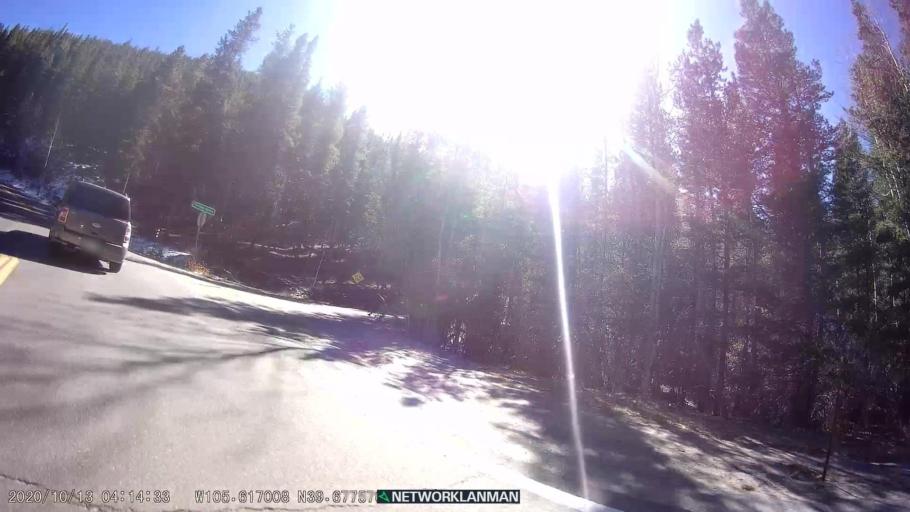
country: US
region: Colorado
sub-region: Clear Creek County
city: Georgetown
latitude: 39.6775
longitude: -105.6169
